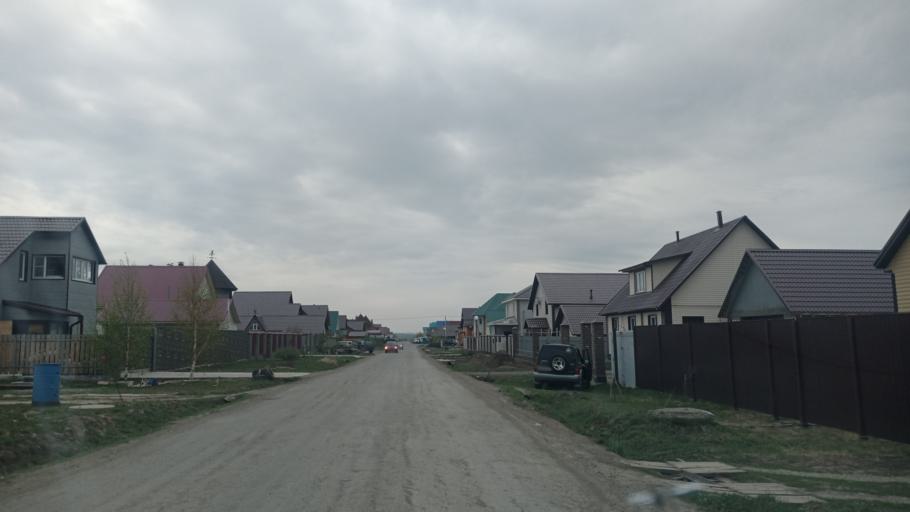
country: RU
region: Altai Krai
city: Yuzhnyy
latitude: 53.2249
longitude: 83.6907
